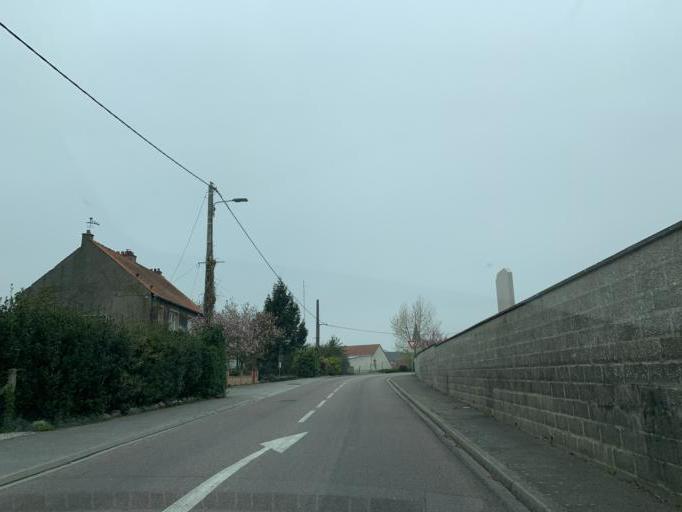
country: FR
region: Nord-Pas-de-Calais
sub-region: Departement du Pas-de-Calais
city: Marquise
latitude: 50.8094
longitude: 1.7085
